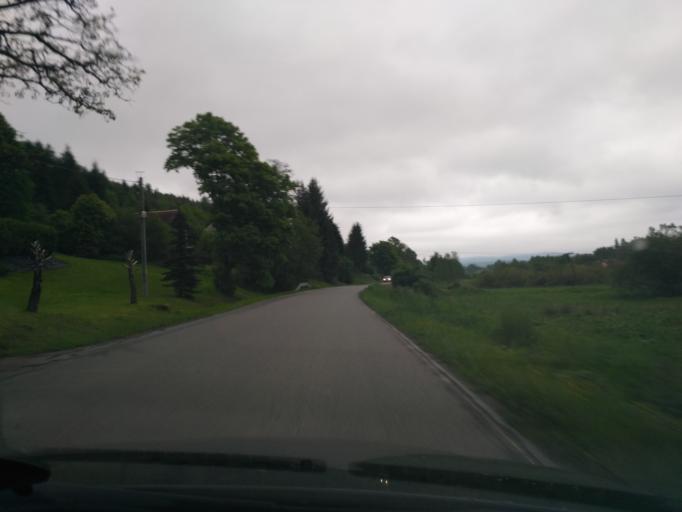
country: PL
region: Subcarpathian Voivodeship
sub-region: Powiat strzyzowski
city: Strzyzow
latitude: 49.8996
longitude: 21.7425
